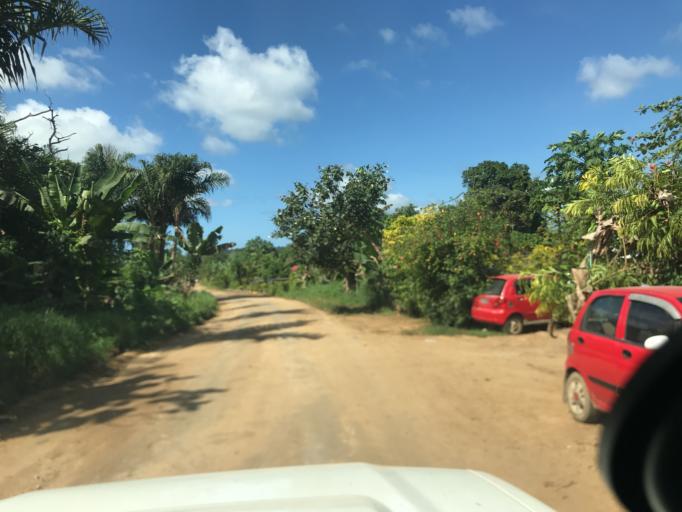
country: VU
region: Sanma
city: Luganville
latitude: -15.5302
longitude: 167.1509
